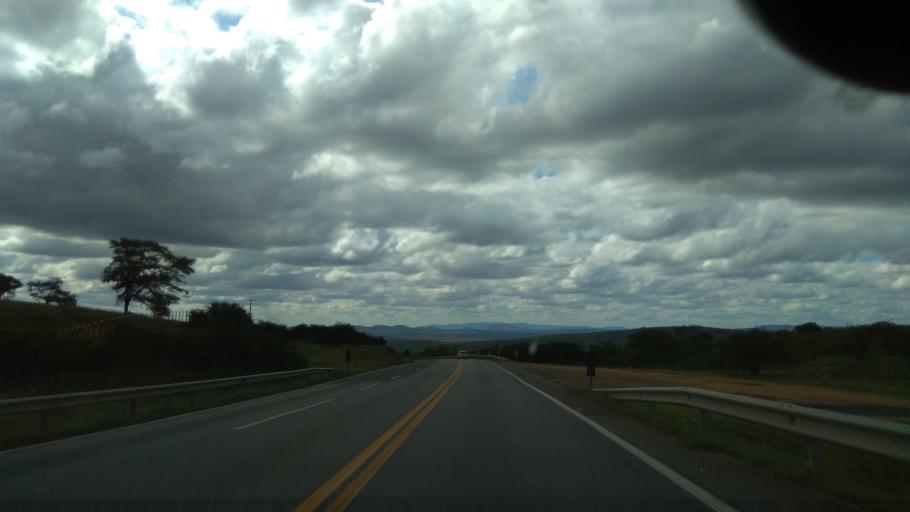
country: BR
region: Bahia
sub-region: Santa Ines
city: Santa Ines
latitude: -13.0619
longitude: -39.9568
